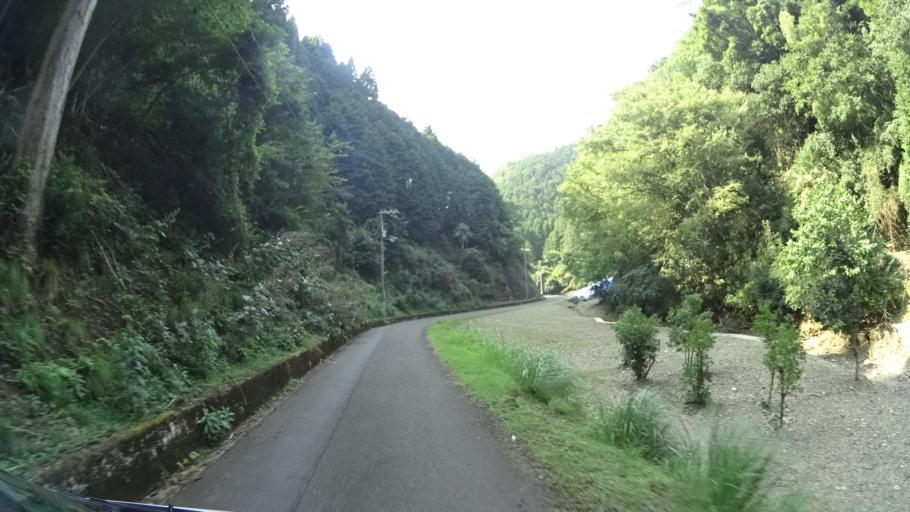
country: JP
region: Kyoto
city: Maizuru
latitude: 35.4051
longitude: 135.2404
